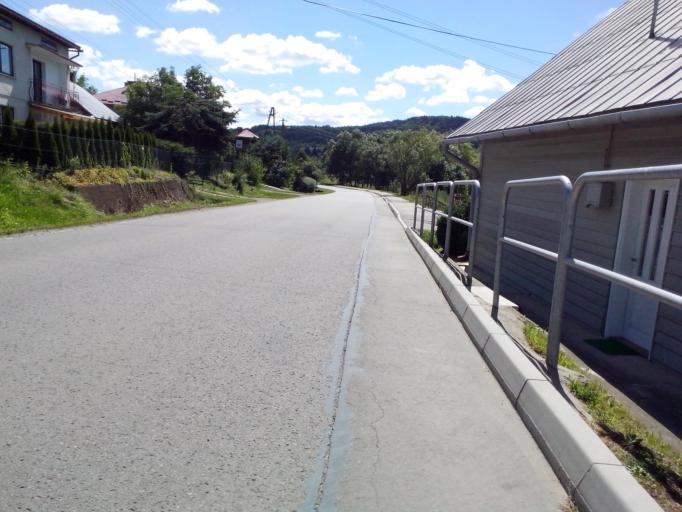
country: PL
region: Subcarpathian Voivodeship
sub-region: Powiat brzozowski
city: Domaradz
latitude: 49.7930
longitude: 21.9521
